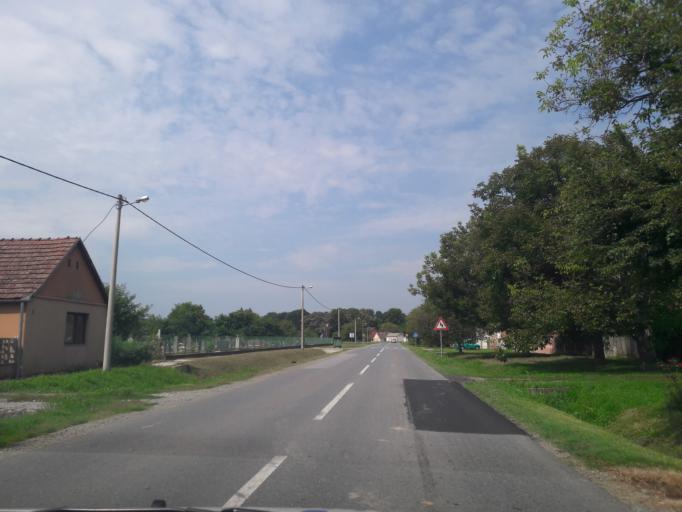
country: HR
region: Osjecko-Baranjska
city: Bizovac
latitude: 45.5149
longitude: 18.4763
